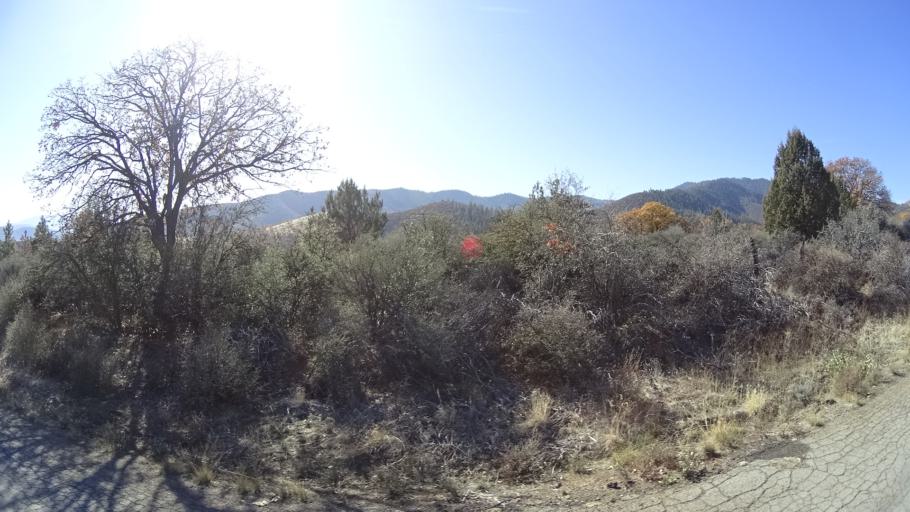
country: US
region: California
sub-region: Siskiyou County
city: Yreka
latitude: 41.7727
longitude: -122.6362
